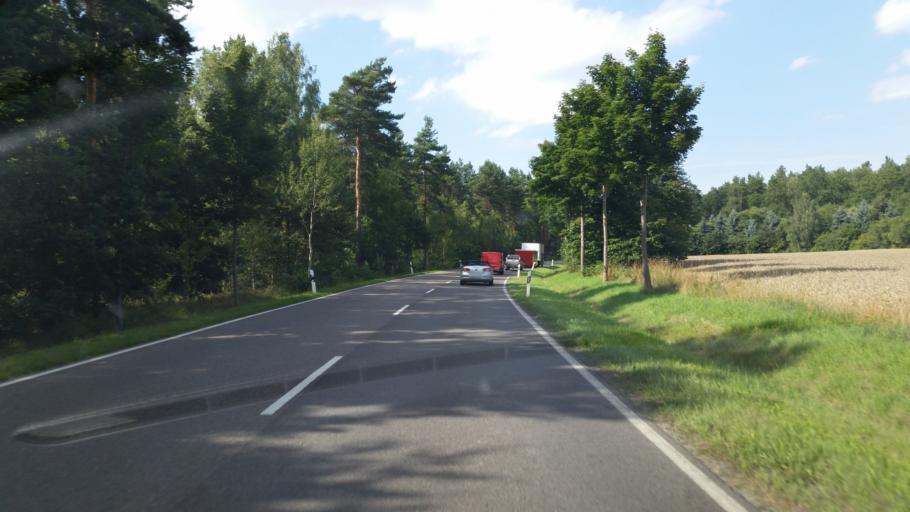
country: DE
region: Saxony
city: Kamenz
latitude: 51.3053
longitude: 14.0932
